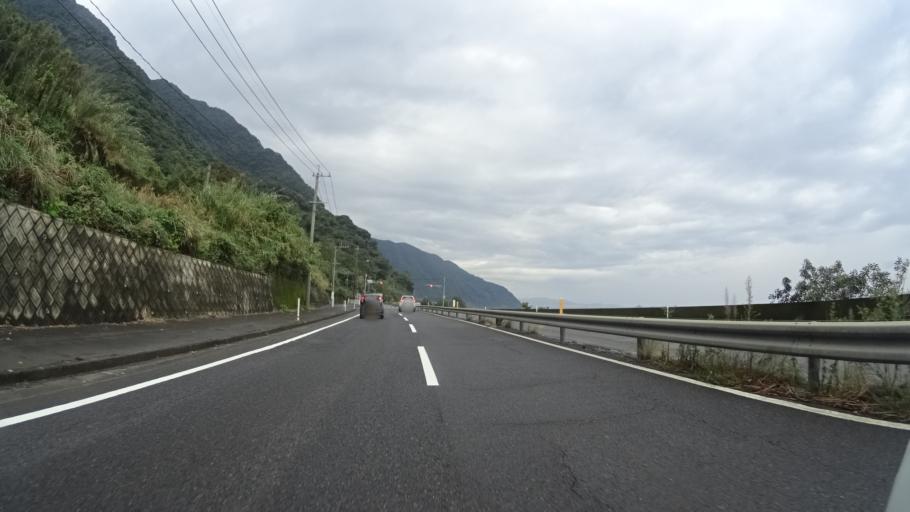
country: JP
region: Kagoshima
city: Kajiki
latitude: 31.6666
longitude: 130.6126
